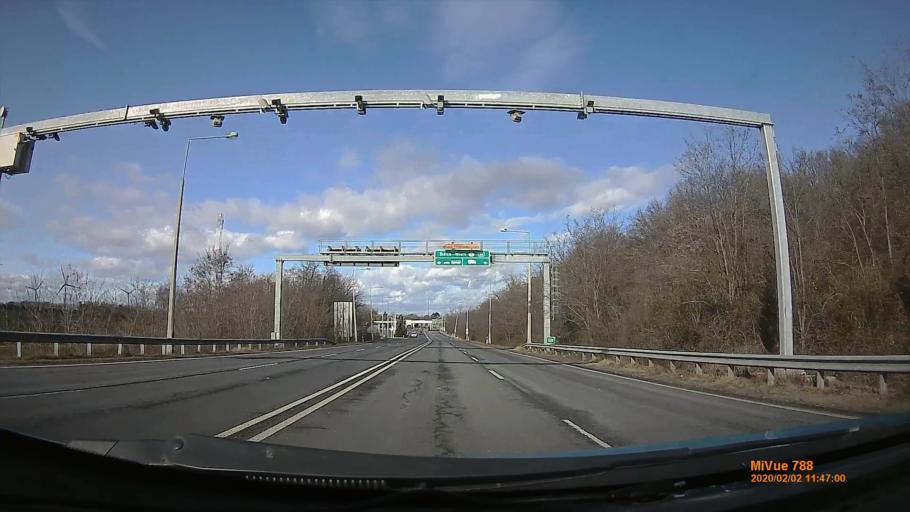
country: AT
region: Burgenland
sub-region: Eisenstadt-Umgebung
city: Klingenbach
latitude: 47.7366
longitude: 16.5495
